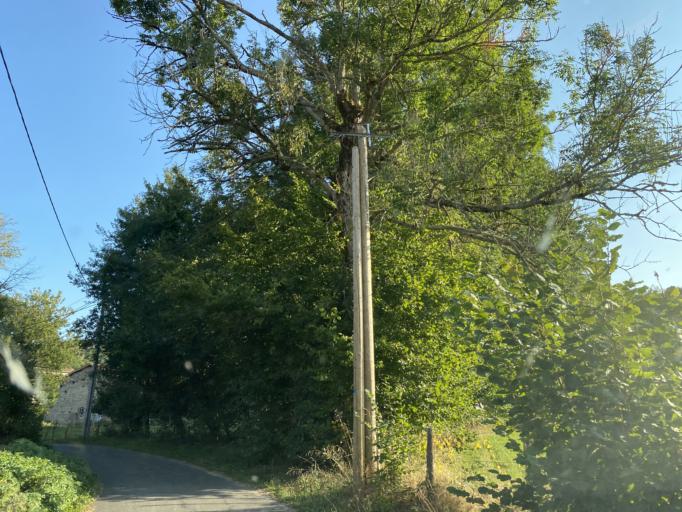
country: FR
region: Rhone-Alpes
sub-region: Departement de la Loire
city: Noiretable
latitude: 45.8017
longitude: 3.7617
